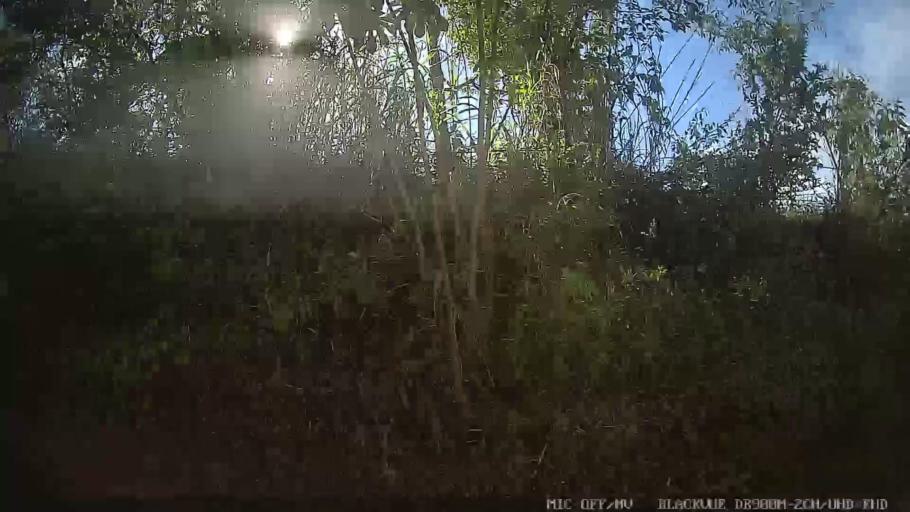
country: BR
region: Sao Paulo
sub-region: Bom Jesus Dos Perdoes
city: Bom Jesus dos Perdoes
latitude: -23.1331
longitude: -46.5019
